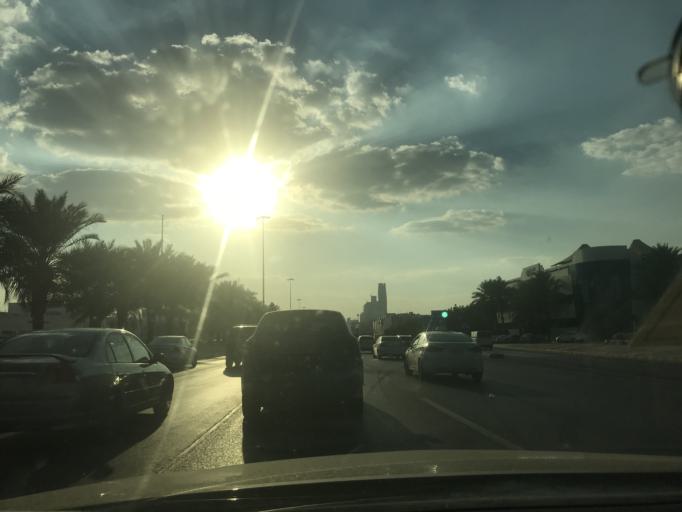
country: SA
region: Ar Riyad
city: Riyadh
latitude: 24.7755
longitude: 46.6809
